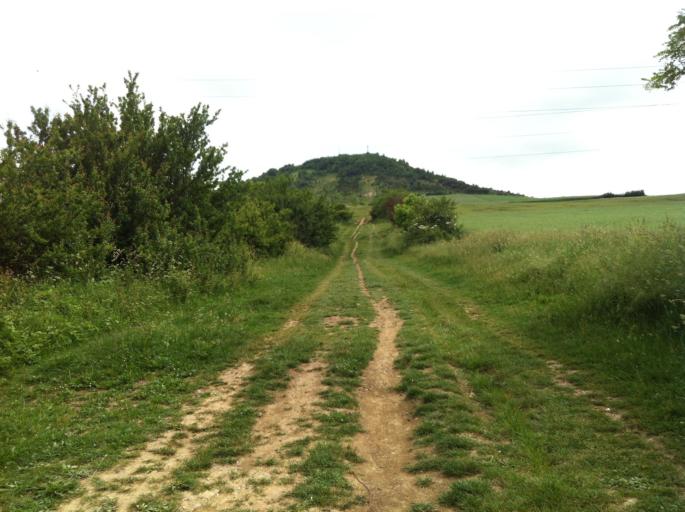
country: ES
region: Basque Country
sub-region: Provincia de Alava
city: Gasteiz / Vitoria
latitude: 42.8242
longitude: -2.6610
